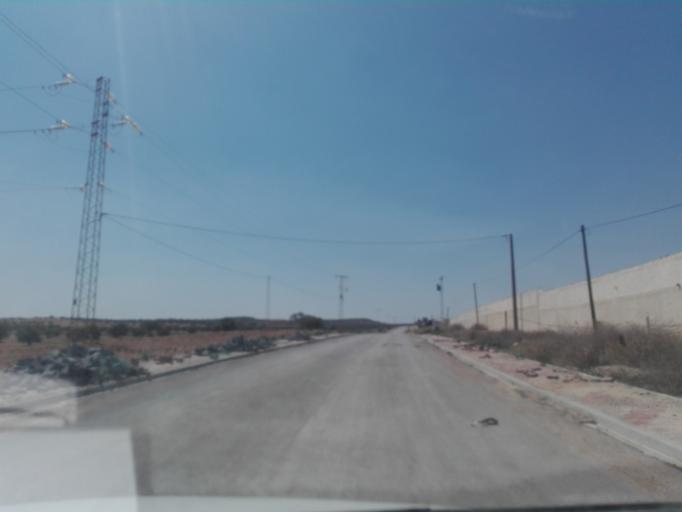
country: TN
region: Safaqis
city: Sfax
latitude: 34.7285
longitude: 10.5237
